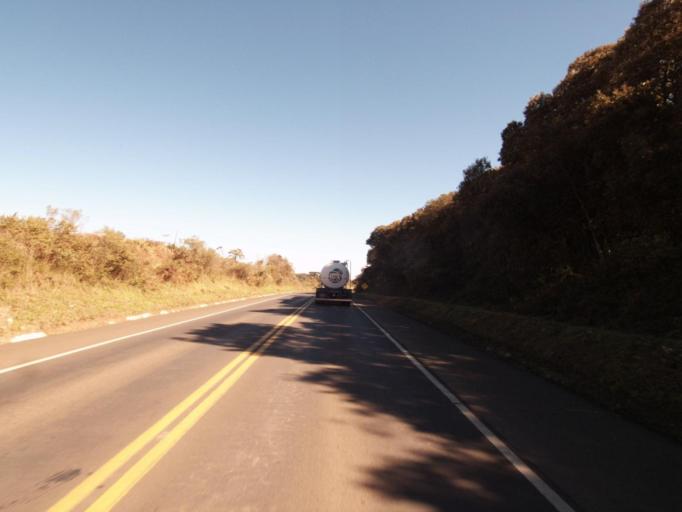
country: BR
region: Santa Catarina
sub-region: Xanxere
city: Xanxere
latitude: -26.8712
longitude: -52.3184
